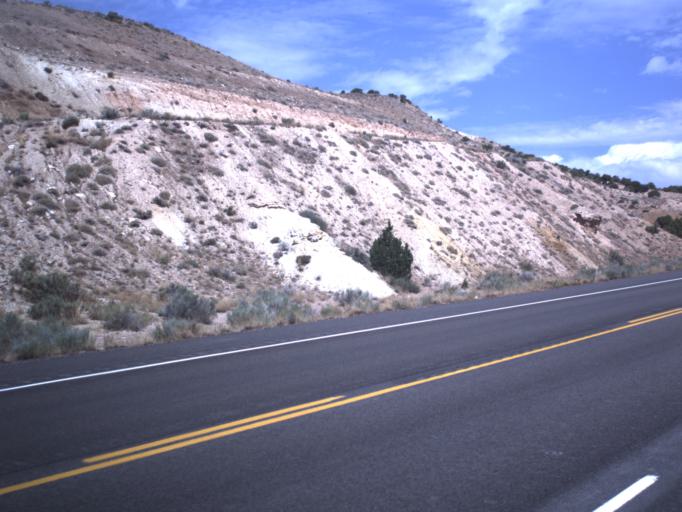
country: US
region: Utah
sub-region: Uintah County
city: Naples
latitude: 40.3389
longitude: -109.4844
